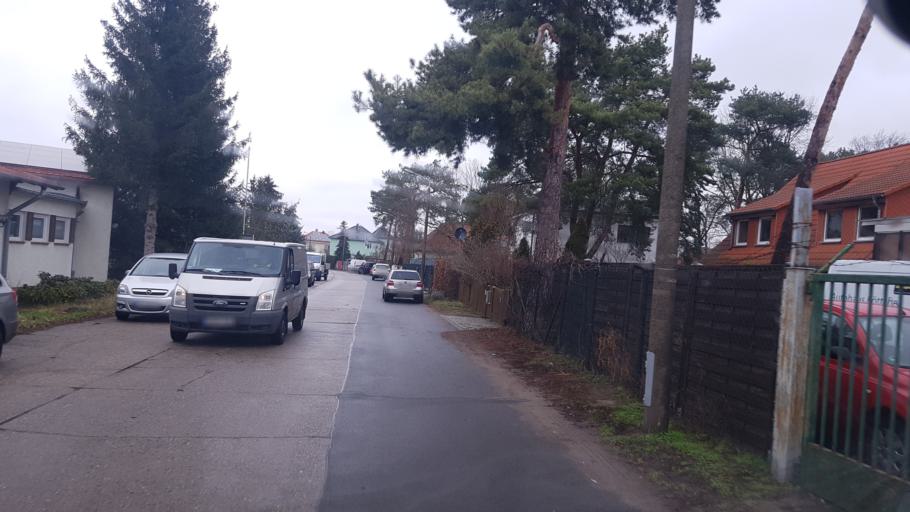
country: DE
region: Berlin
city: Wannsee
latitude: 52.3572
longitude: 13.1301
